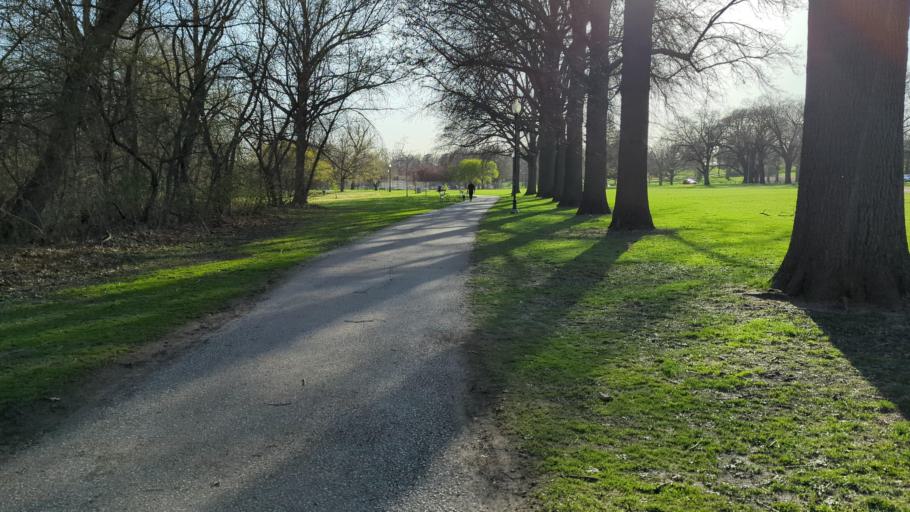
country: US
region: Nebraska
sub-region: Douglas County
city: Ralston
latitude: 41.2523
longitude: -96.0096
